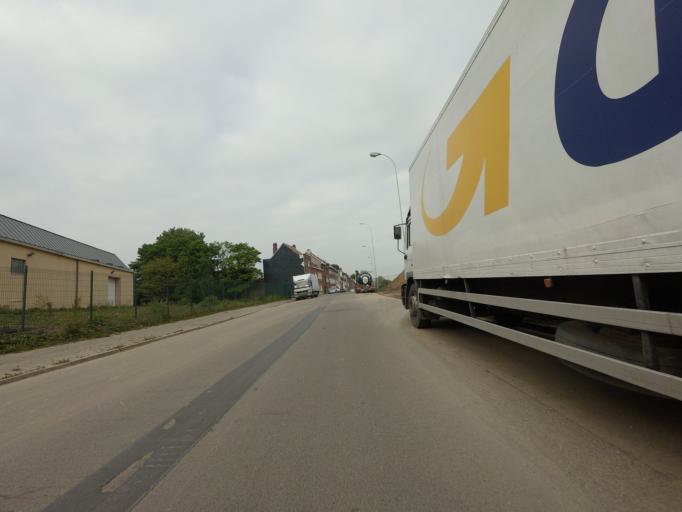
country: BE
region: Flanders
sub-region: Provincie Vlaams-Brabant
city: Diegem
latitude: 50.8857
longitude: 4.4268
